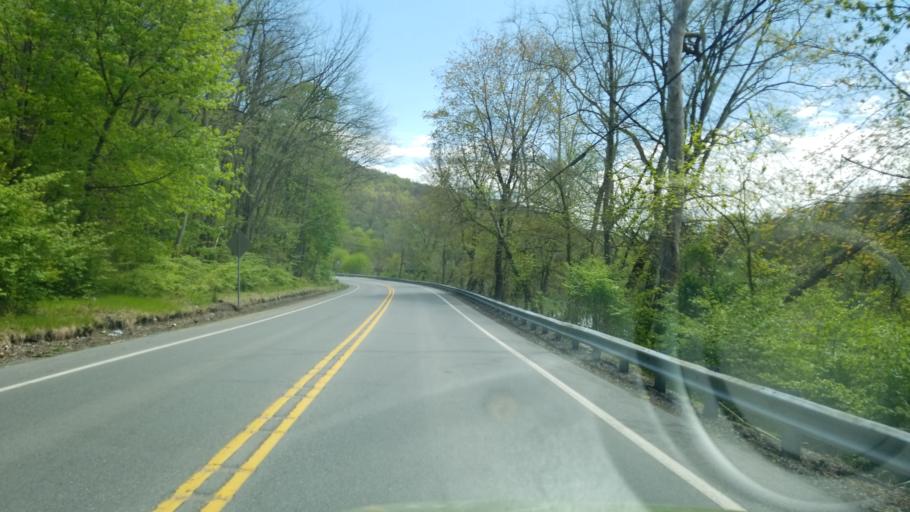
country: US
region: Pennsylvania
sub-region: Huntingdon County
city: Mount Union
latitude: 40.3969
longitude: -77.9397
